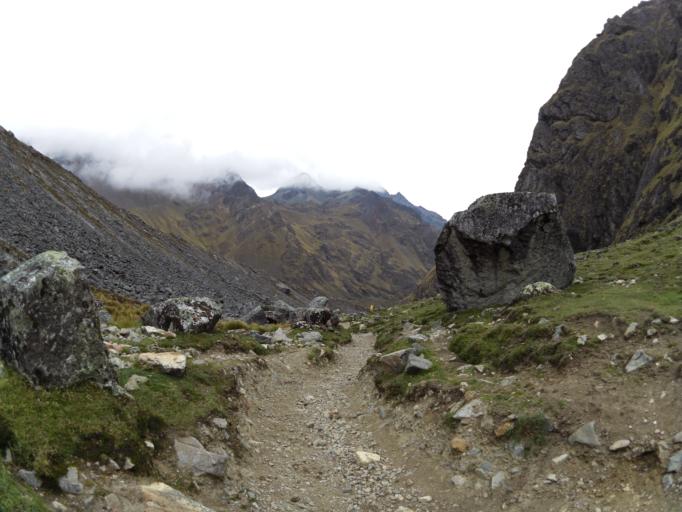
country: PE
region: Cusco
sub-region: Provincia de Anta
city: Limatambo
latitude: -13.3581
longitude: -72.5600
